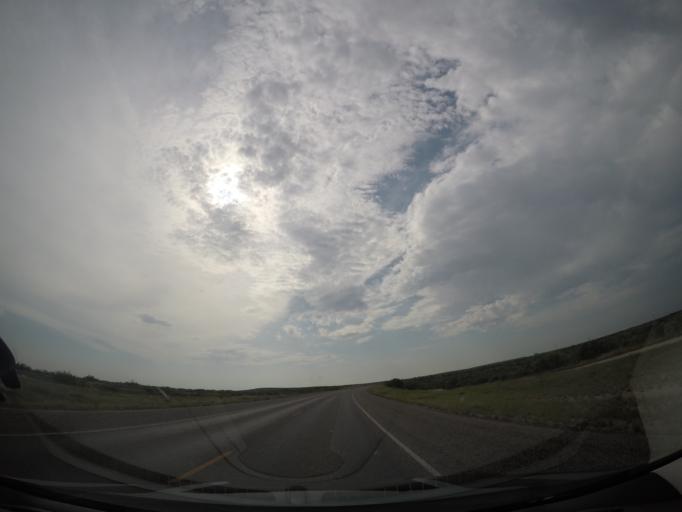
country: US
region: Texas
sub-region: Val Verde County
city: Cienegas Terrace
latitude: 29.7838
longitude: -101.4070
